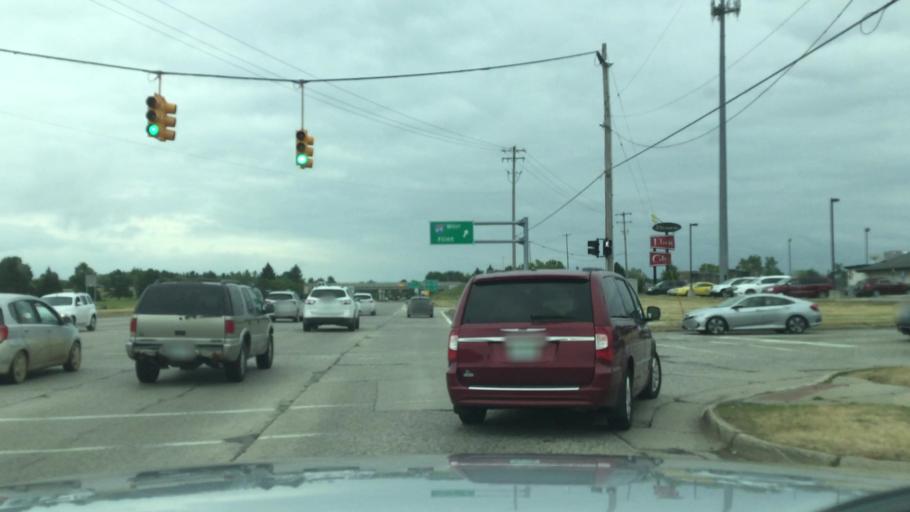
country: US
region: Michigan
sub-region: Genesee County
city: Davison
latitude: 43.0148
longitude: -83.5177
